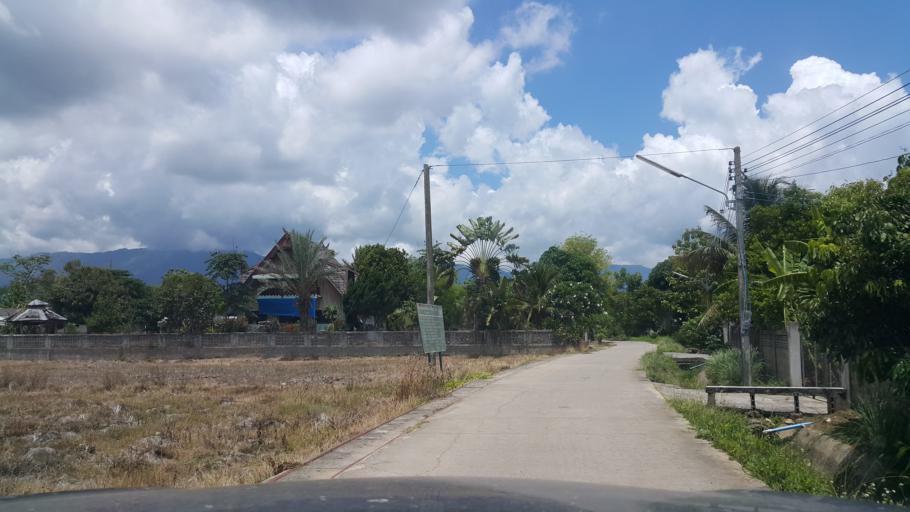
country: TH
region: Phayao
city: Phayao
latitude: 19.1802
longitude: 99.8450
